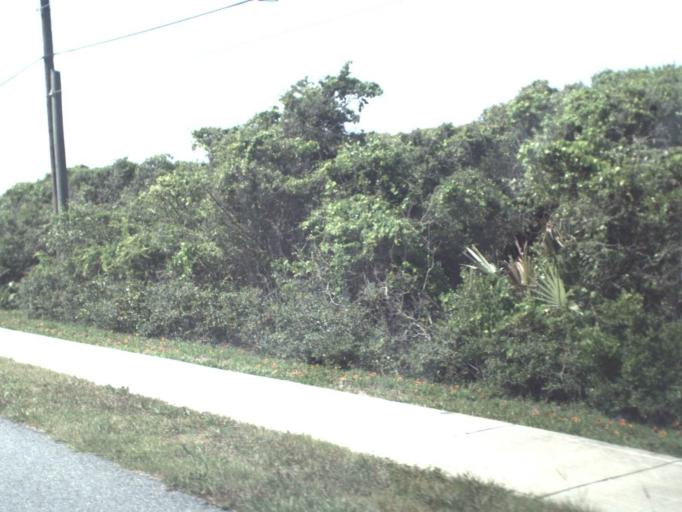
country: US
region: Florida
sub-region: Saint Johns County
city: Butler Beach
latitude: 29.7188
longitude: -81.2341
